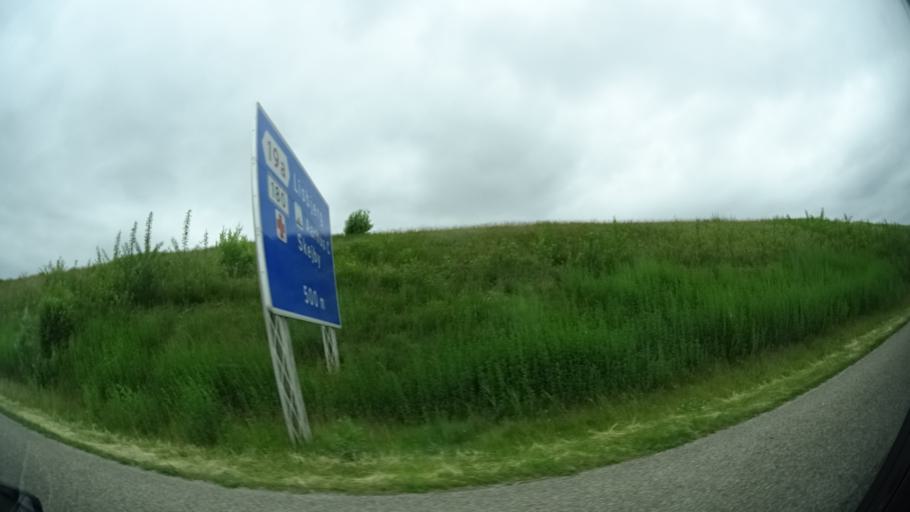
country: DK
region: Central Jutland
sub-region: Arhus Kommune
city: Trige
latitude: 56.2159
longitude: 10.1808
